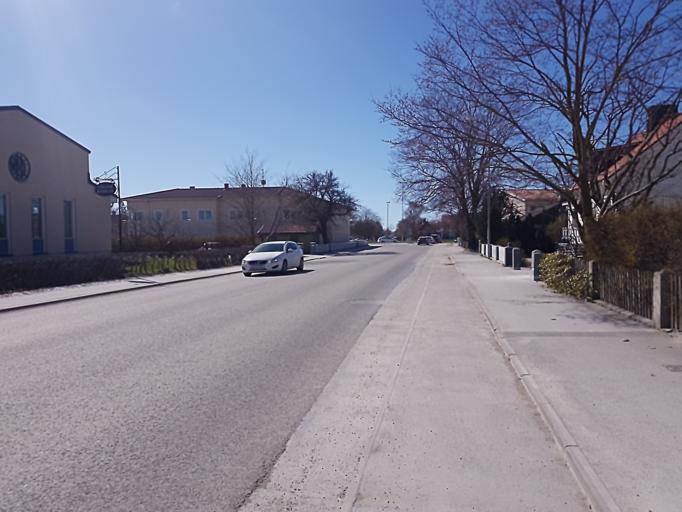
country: SE
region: Gotland
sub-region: Gotland
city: Visby
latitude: 57.6361
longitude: 18.3088
